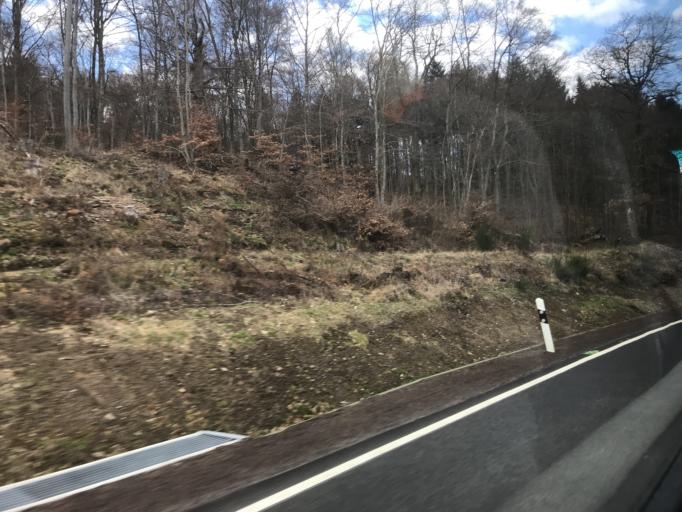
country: DE
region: Rheinland-Pfalz
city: Glees
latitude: 50.4111
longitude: 7.2542
